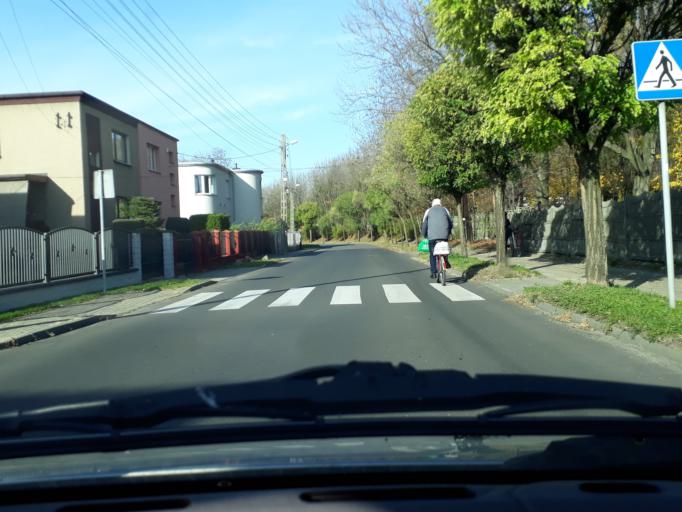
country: PL
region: Silesian Voivodeship
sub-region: Powiat tarnogorski
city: Tarnowskie Gory
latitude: 50.4357
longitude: 18.8655
